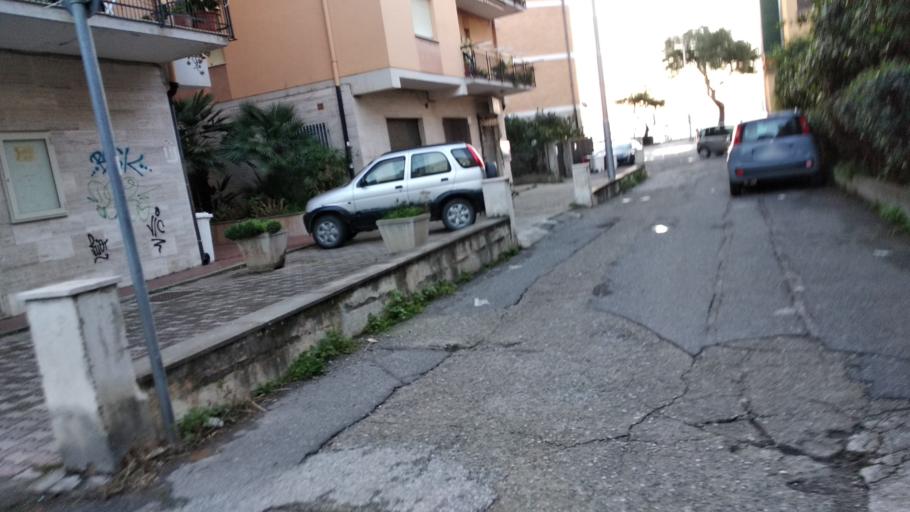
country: IT
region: Calabria
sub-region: Provincia di Catanzaro
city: Barone
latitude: 38.8275
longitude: 16.6262
